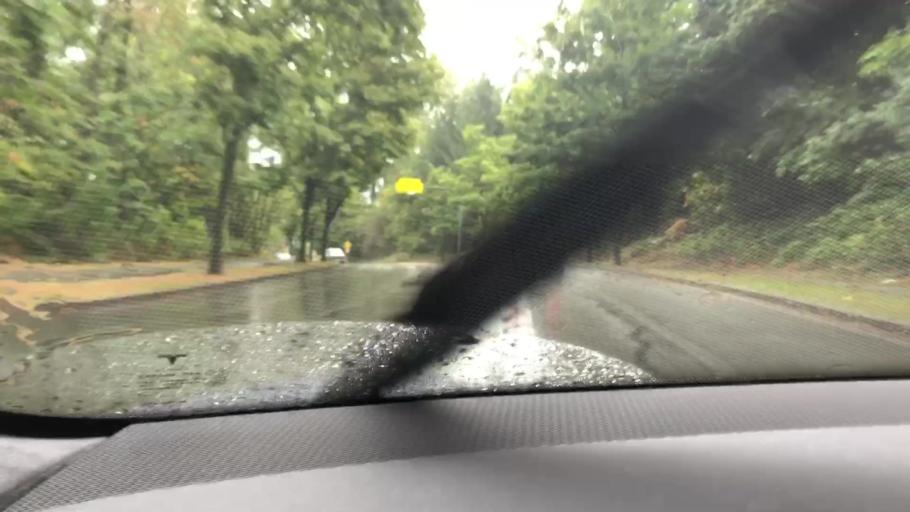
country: CA
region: British Columbia
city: New Westminster
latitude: 49.2348
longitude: -122.9122
